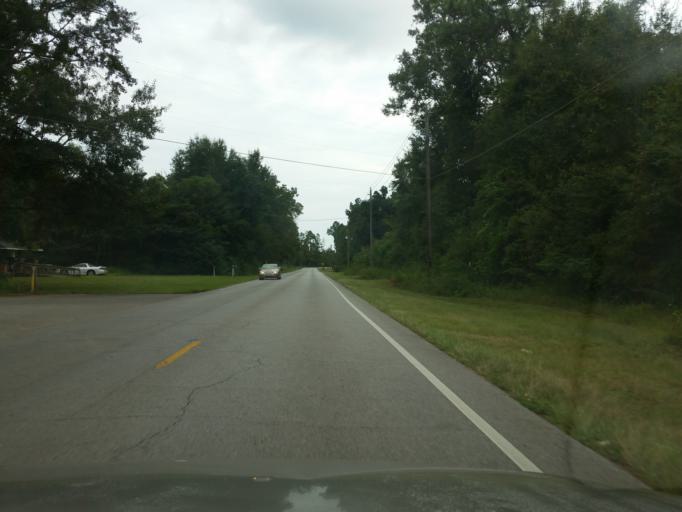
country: US
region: Florida
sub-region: Escambia County
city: Molino
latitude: 30.6816
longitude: -87.3218
